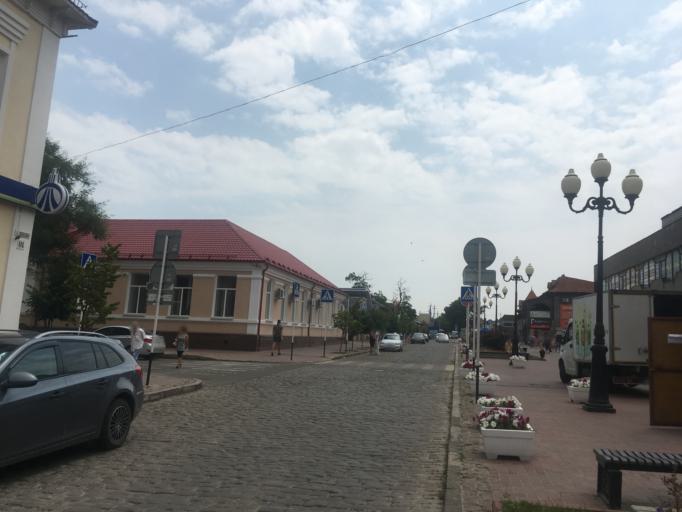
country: RU
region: Krasnodarskiy
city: Yeysk
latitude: 46.7108
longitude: 38.2774
